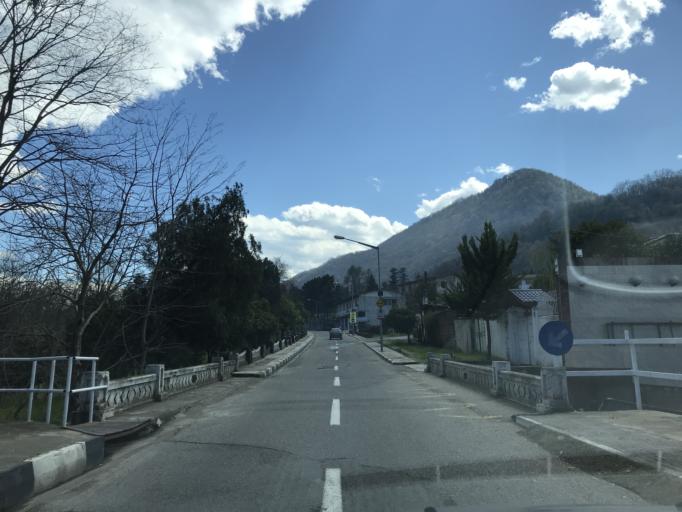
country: IR
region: Mazandaran
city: Ramsar
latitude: 36.9068
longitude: 50.6531
